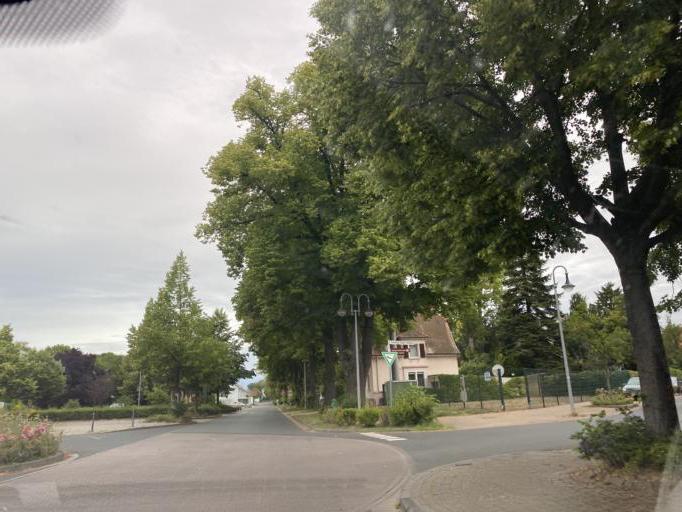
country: DE
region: Rheinland-Pfalz
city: Sprendlingen
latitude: 49.8591
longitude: 7.9822
